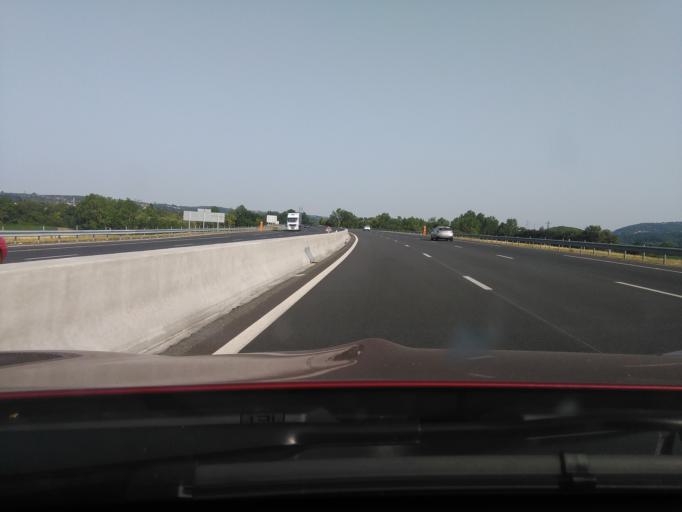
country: FR
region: Rhone-Alpes
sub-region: Departement du Rhone
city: Quincieux
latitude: 45.9065
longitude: 4.7992
